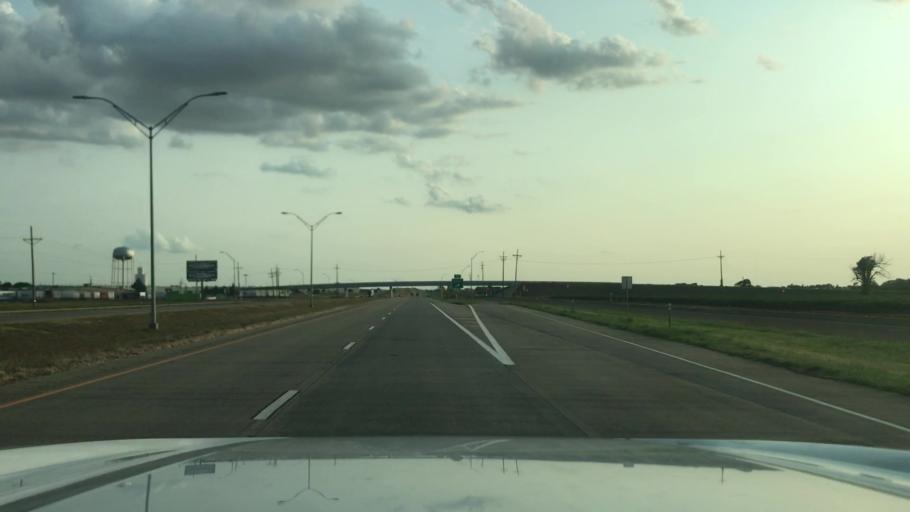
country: US
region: Texas
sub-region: Hale County
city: Seth Ward
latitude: 34.2221
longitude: -101.7224
